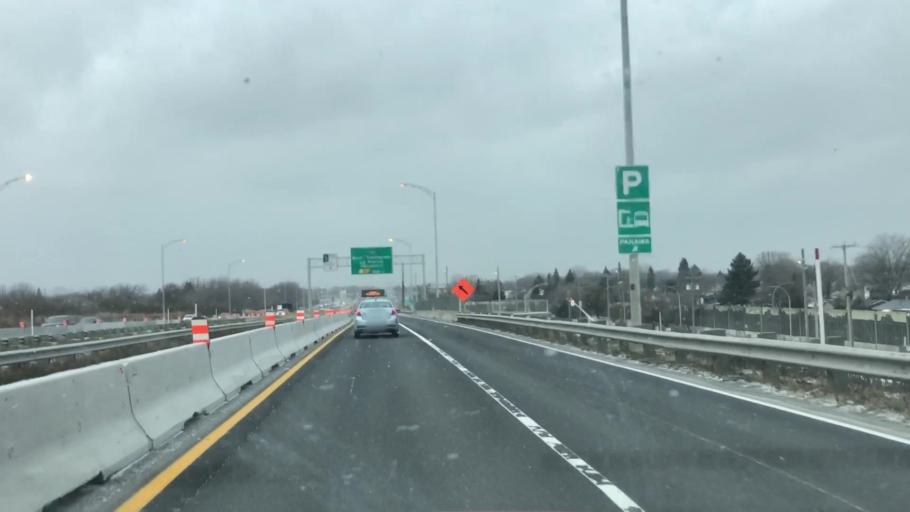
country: CA
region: Quebec
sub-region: Monteregie
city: Brossard
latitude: 45.4568
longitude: -73.4472
